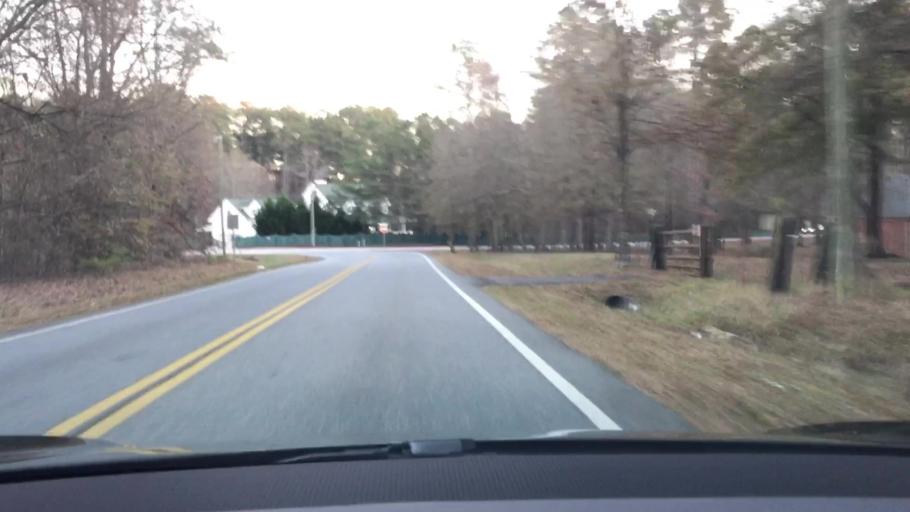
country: US
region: Georgia
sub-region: Walton County
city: Loganville
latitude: 33.8779
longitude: -83.9118
